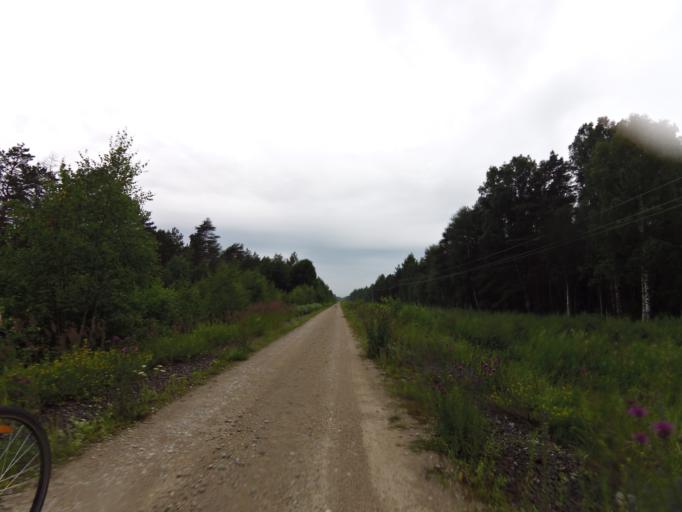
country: EE
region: Harju
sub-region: Nissi vald
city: Turba
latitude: 58.9917
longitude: 24.0079
